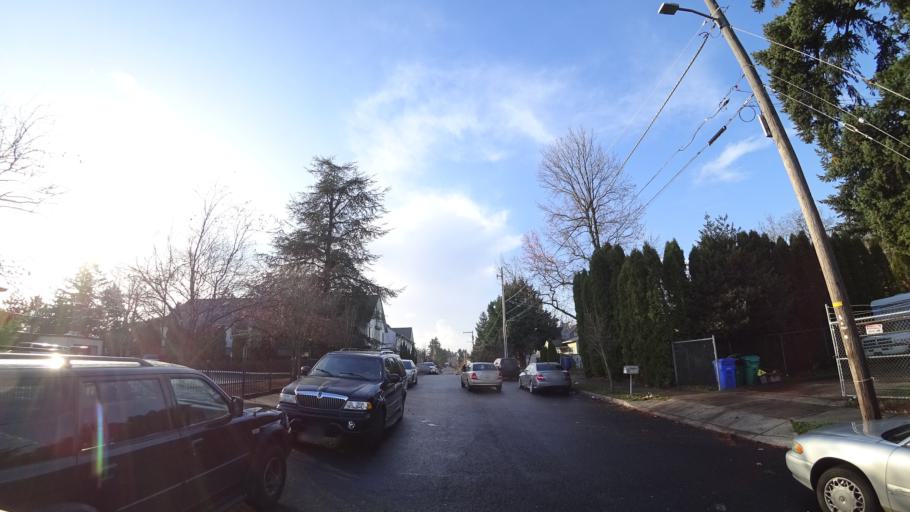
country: US
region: Oregon
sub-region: Multnomah County
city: Lents
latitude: 45.5211
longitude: -122.5381
